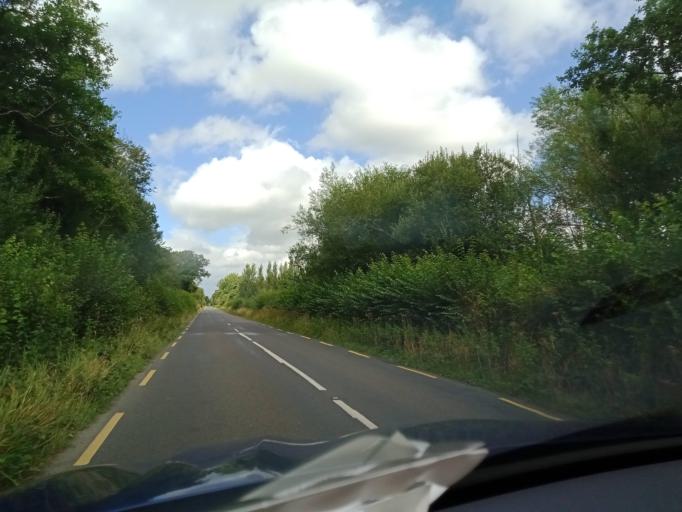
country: IE
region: Leinster
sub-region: Laois
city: Portlaoise
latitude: 52.9830
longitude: -7.2878
